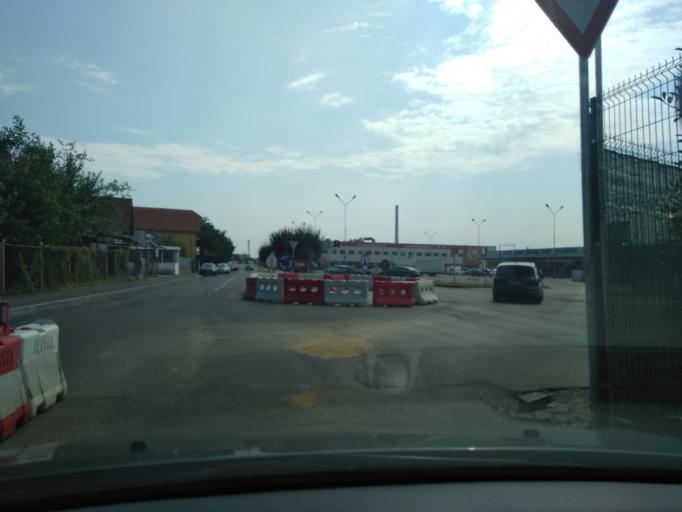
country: RO
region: Gorj
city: Targu Jiu
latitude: 45.0304
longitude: 23.2660
